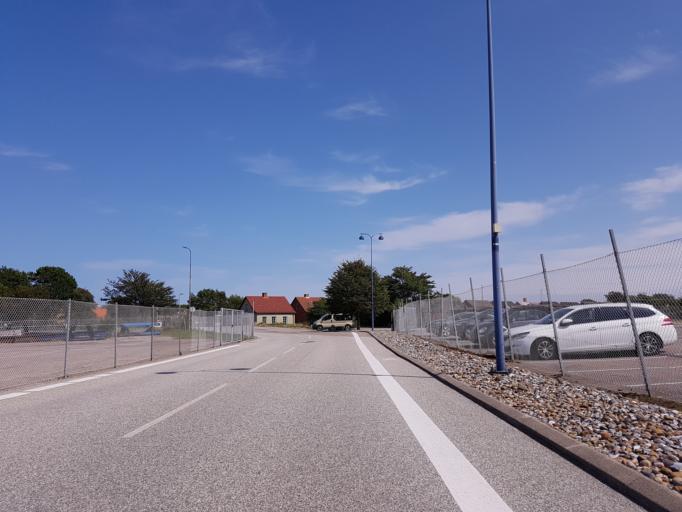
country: DK
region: Zealand
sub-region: Guldborgsund Kommune
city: Nykobing Falster
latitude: 54.5739
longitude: 11.9285
